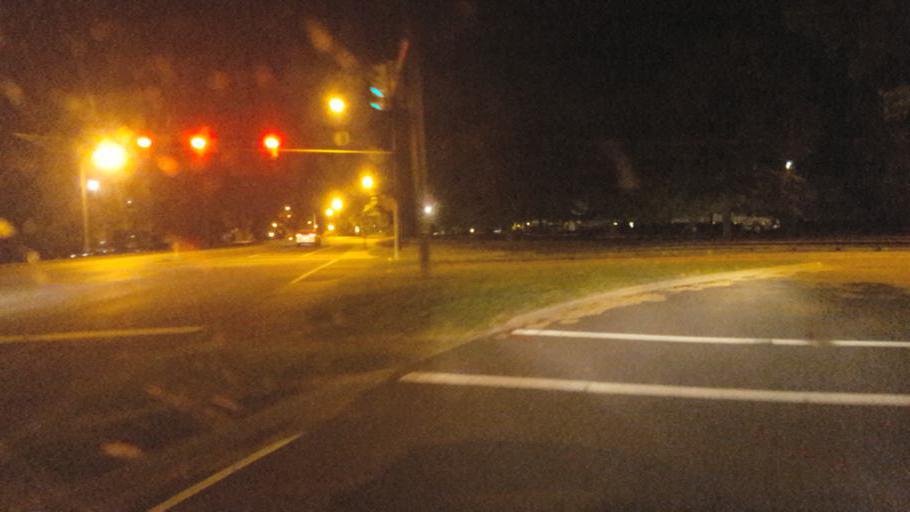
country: US
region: Virginia
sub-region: Fairfax County
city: Lincolnia
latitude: 38.8135
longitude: -77.1304
